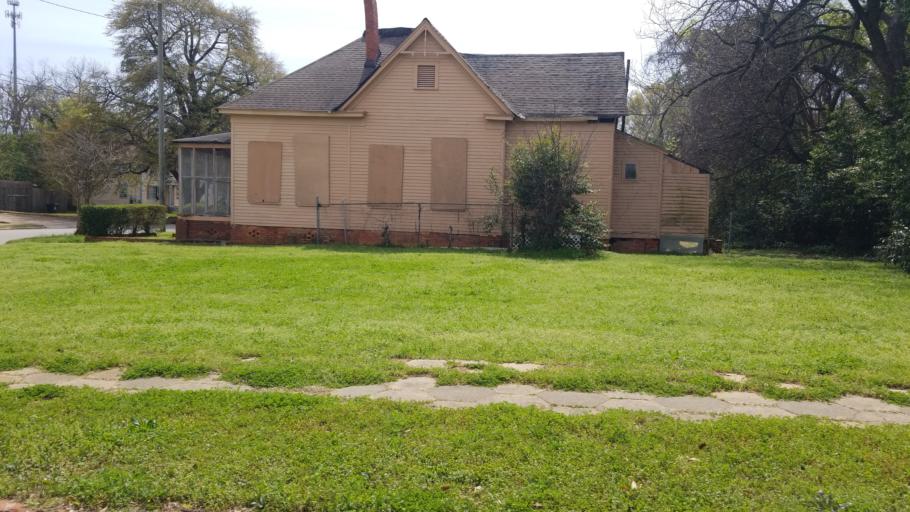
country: US
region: Alabama
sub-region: Montgomery County
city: Montgomery
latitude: 32.3710
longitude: -86.3123
